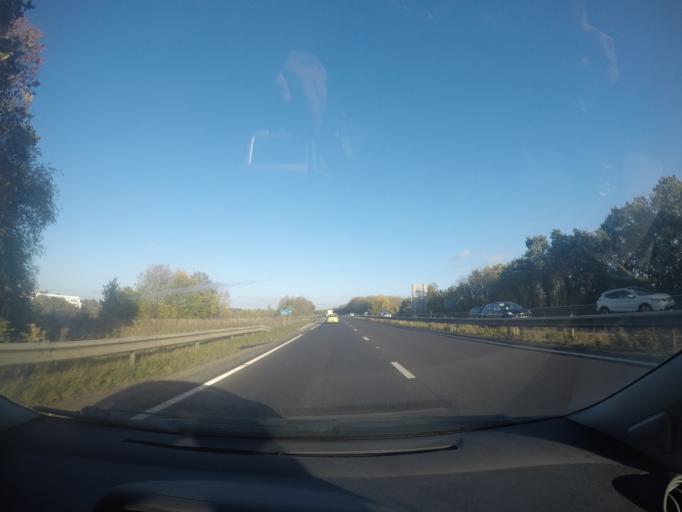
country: GB
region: England
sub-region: City of York
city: Bishopthorpe
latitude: 53.9244
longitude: -1.1164
